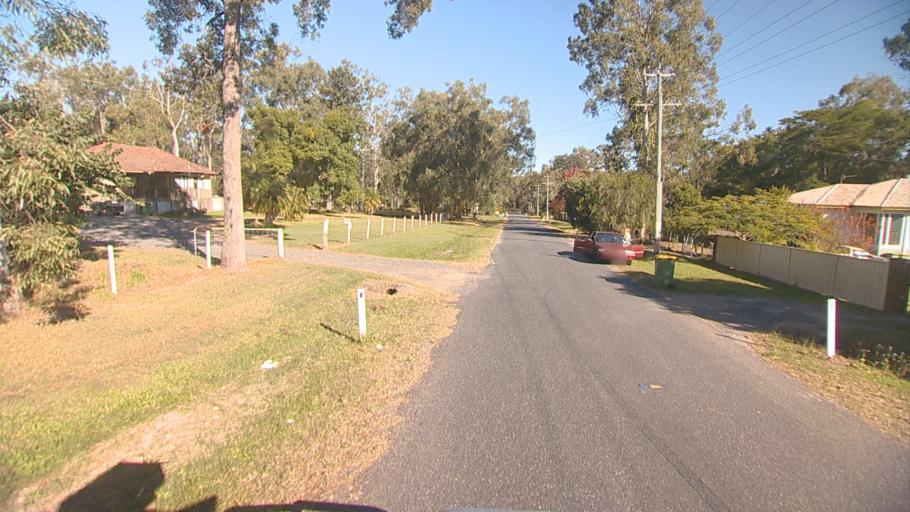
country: AU
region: Queensland
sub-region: Logan
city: Park Ridge South
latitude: -27.7303
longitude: 153.0115
